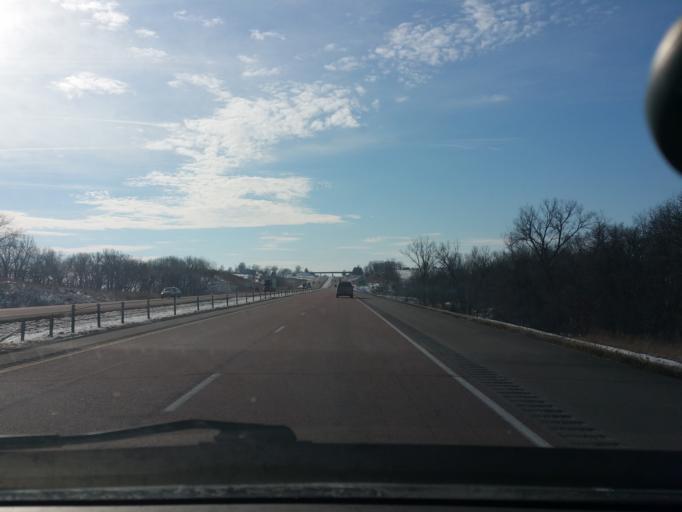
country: US
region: Iowa
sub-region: Warren County
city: Norwalk
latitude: 41.3035
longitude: -93.7792
